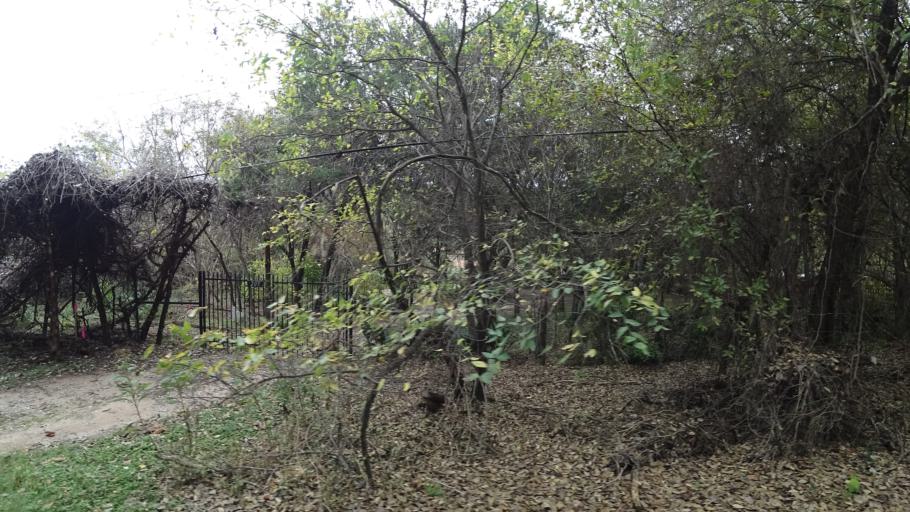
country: US
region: Texas
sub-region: Travis County
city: Bee Cave
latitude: 30.3527
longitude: -97.9202
